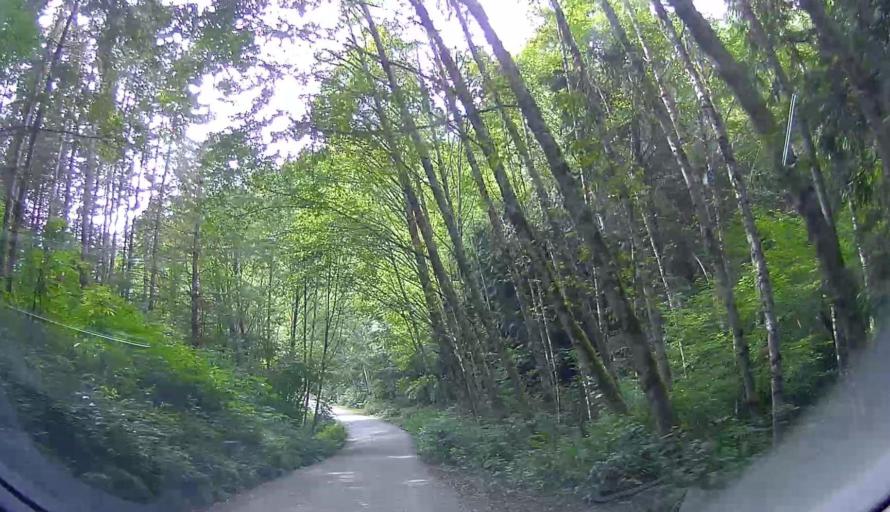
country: US
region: Washington
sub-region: Whatcom County
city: Sudden Valley
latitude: 48.6145
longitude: -122.3876
